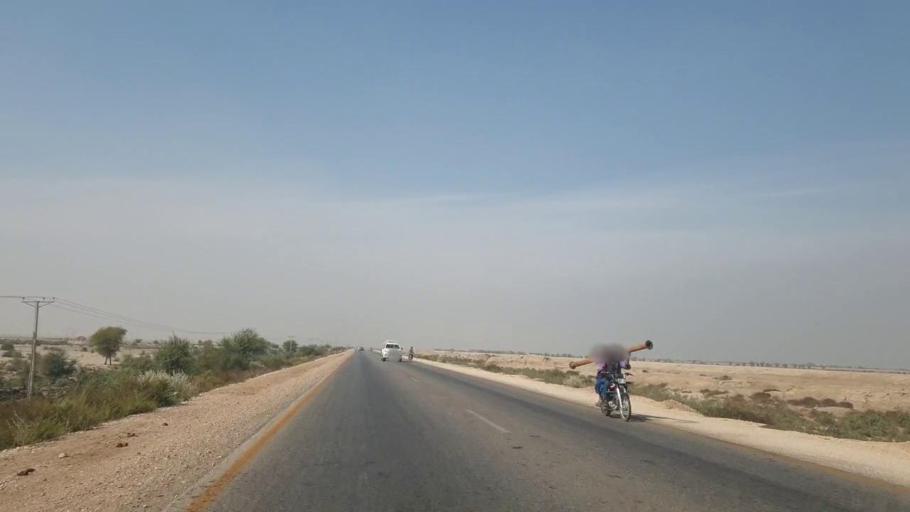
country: PK
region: Sindh
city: Sann
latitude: 25.9078
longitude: 68.2272
